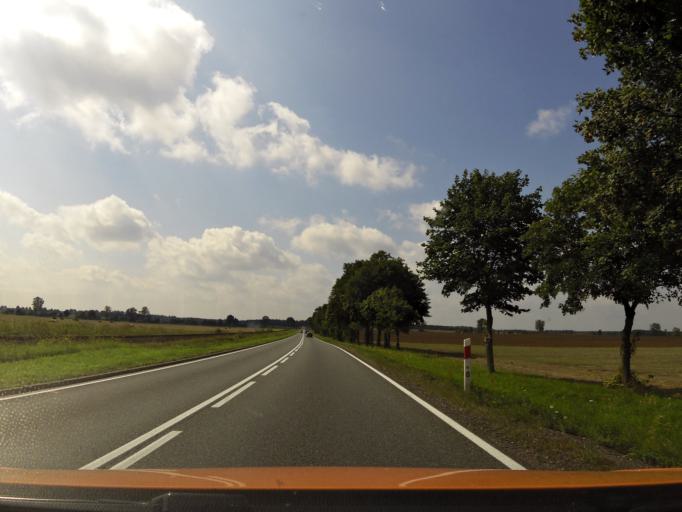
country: PL
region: West Pomeranian Voivodeship
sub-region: Powiat goleniowski
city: Nowogard
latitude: 53.7088
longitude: 15.1767
